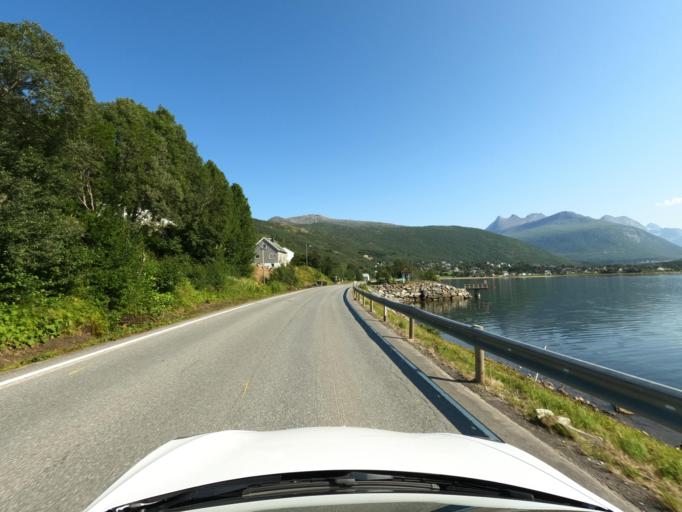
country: NO
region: Nordland
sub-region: Narvik
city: Narvik
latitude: 68.3829
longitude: 17.5852
